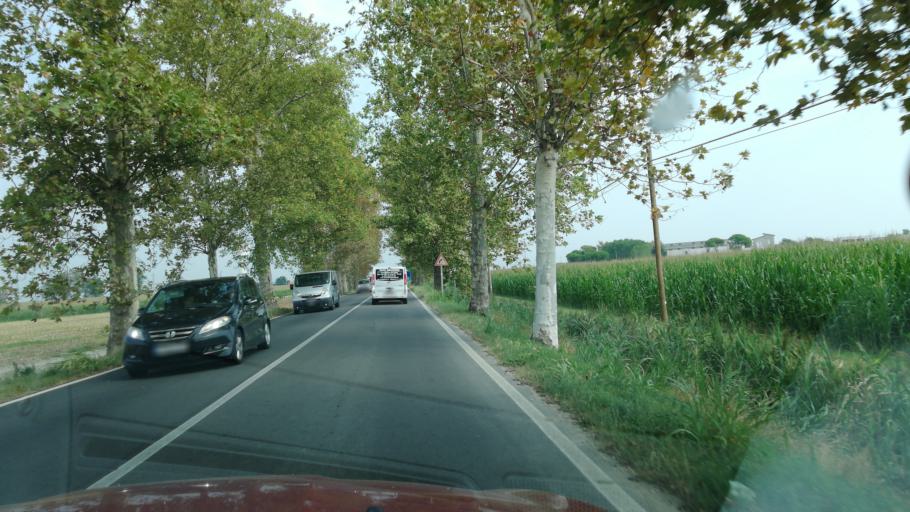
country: IT
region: Veneto
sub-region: Provincia di Venezia
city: La Salute di Livenza
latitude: 45.6654
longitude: 12.8037
